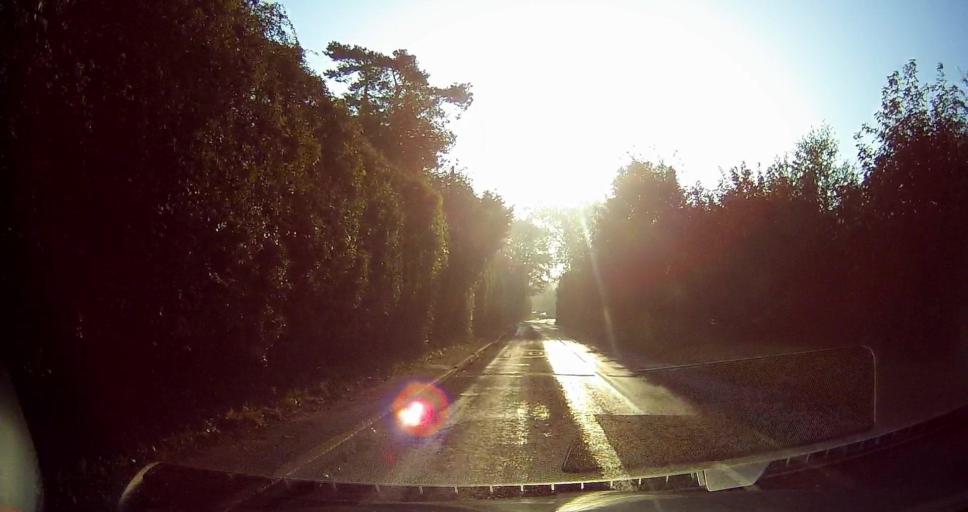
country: GB
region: England
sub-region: Kent
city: Wye
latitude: 51.1824
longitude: 0.9138
